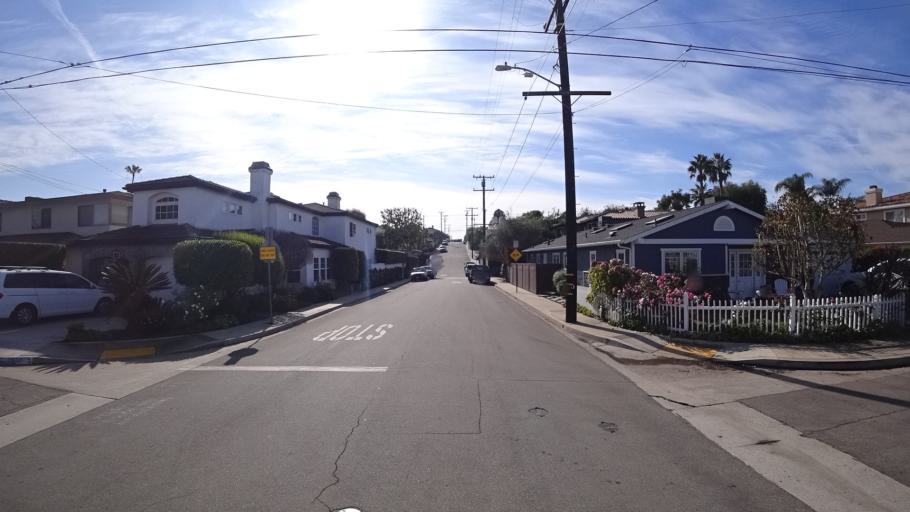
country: US
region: California
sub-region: Los Angeles County
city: Hermosa Beach
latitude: 33.8819
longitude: -118.3874
